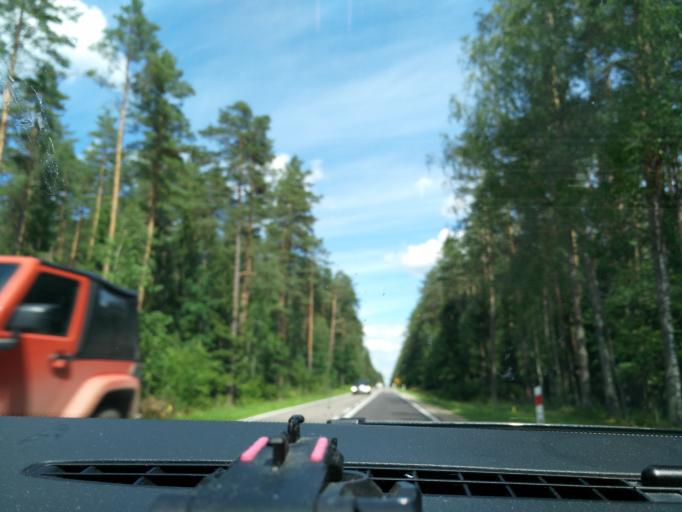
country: PL
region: Podlasie
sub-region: Powiat sejnenski
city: Krasnopol
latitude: 53.9619
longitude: 23.2316
